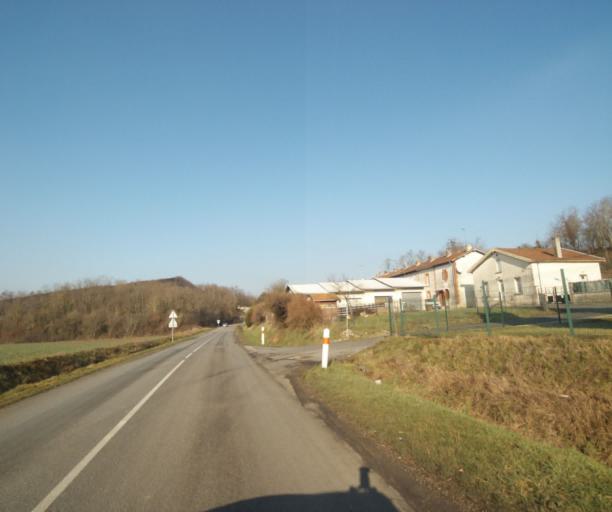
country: FR
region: Champagne-Ardenne
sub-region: Departement de la Haute-Marne
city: Wassy
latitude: 48.4838
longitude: 4.9693
